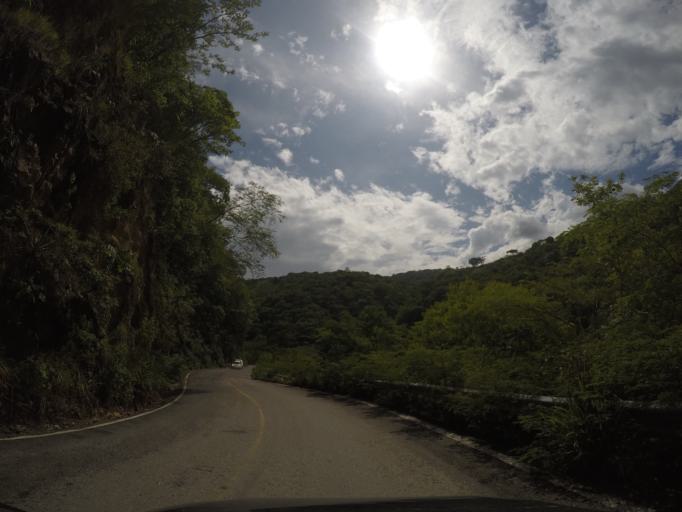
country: MX
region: Oaxaca
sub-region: San Jeronimo Coatlan
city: San Cristobal Honduras
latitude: 16.3711
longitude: -97.0881
